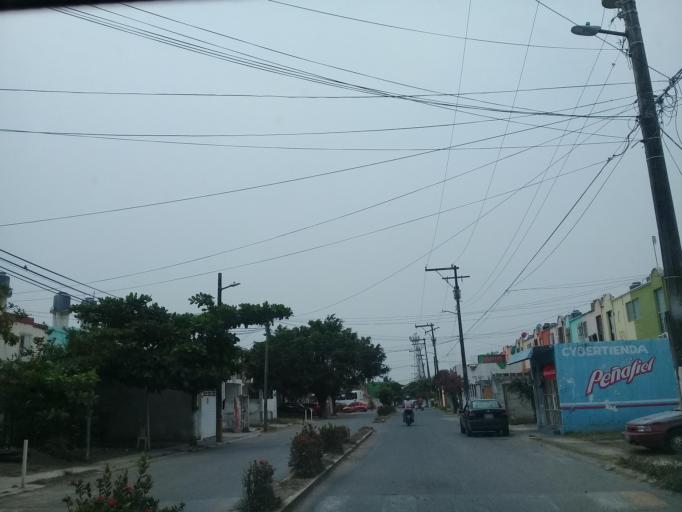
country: MX
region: Veracruz
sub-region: Veracruz
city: Las Amapolas
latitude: 19.1537
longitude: -96.2045
